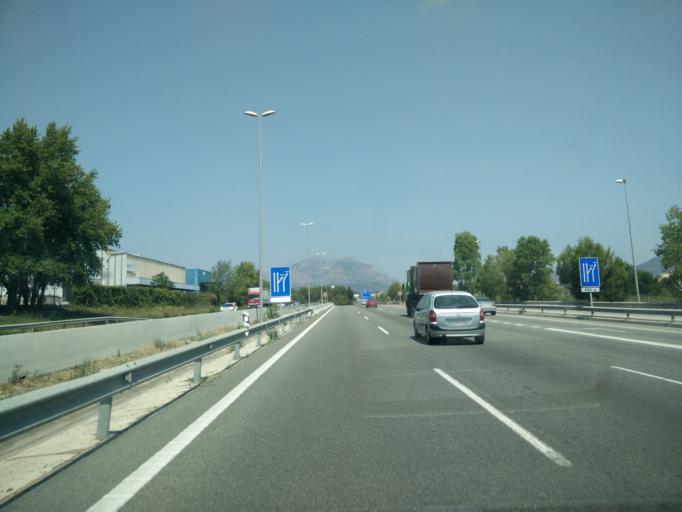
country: ES
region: Catalonia
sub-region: Provincia de Barcelona
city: Abrera
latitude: 41.5098
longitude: 1.9023
